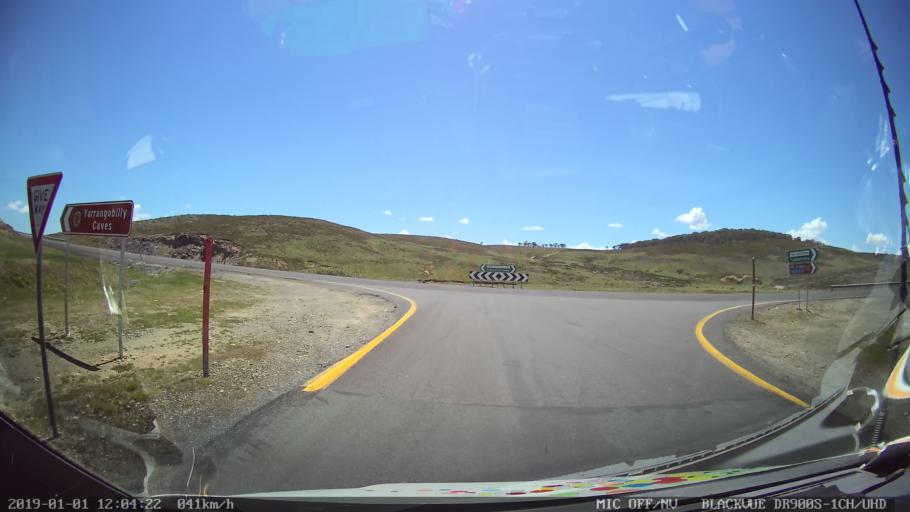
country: AU
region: New South Wales
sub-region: Snowy River
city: Jindabyne
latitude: -35.8667
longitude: 148.4966
